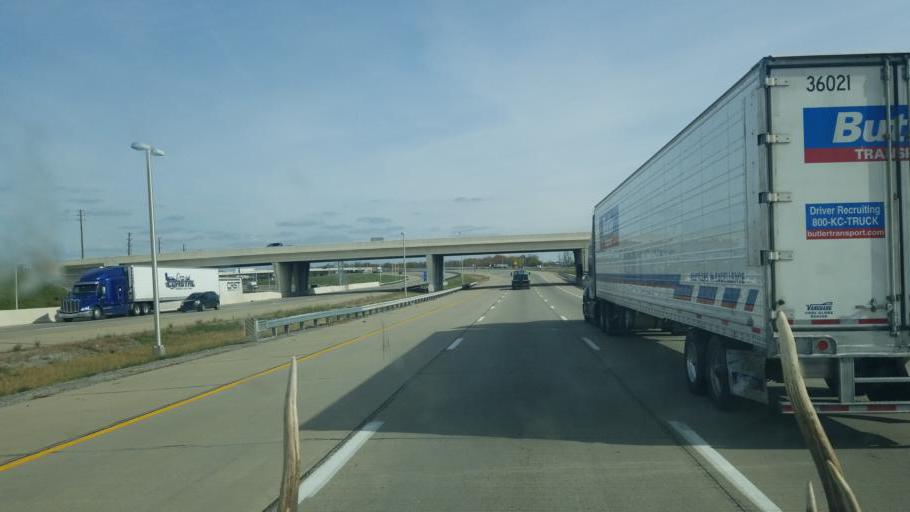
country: US
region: Indiana
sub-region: Marion County
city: Speedway
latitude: 39.7117
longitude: -86.2711
